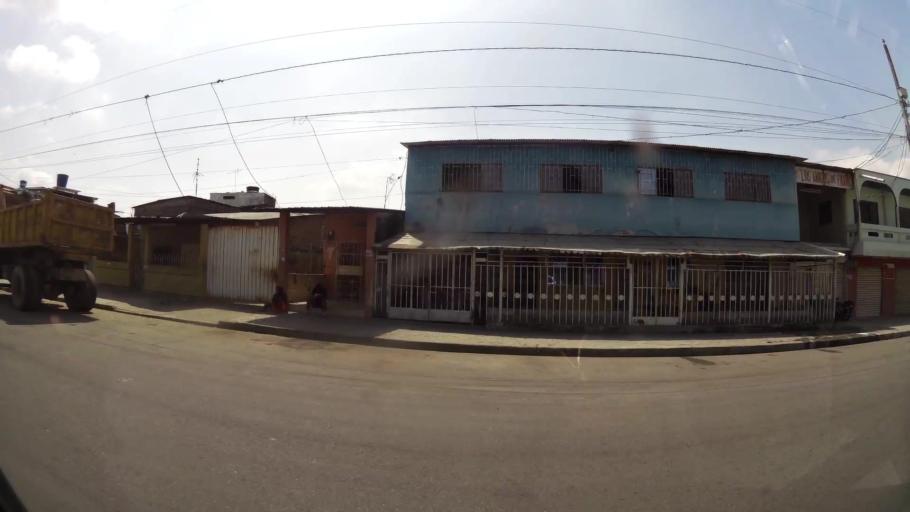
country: EC
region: Guayas
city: Eloy Alfaro
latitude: -2.1550
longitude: -79.8373
